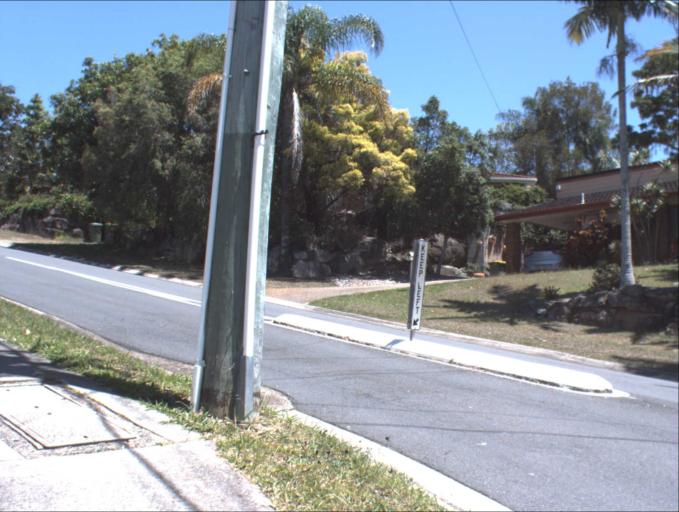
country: AU
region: Queensland
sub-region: Logan
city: Springwood
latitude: -27.6043
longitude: 153.1320
